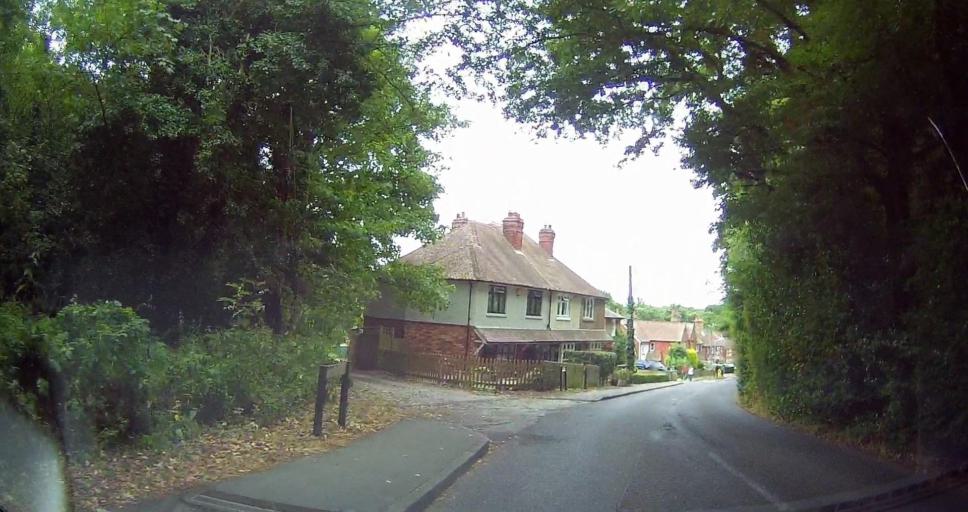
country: GB
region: England
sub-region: East Sussex
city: Wadhurst
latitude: 51.0933
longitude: 0.3877
